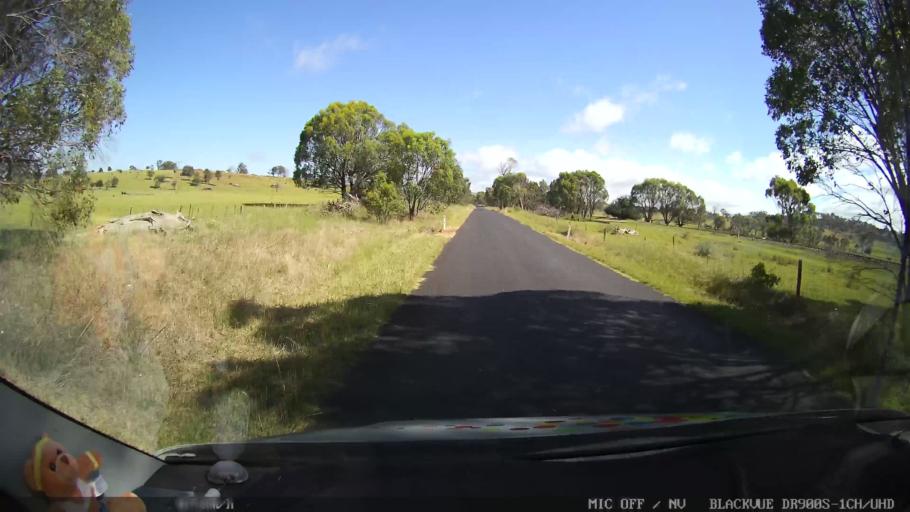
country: AU
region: New South Wales
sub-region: Guyra
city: Guyra
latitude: -30.0844
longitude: 151.6776
